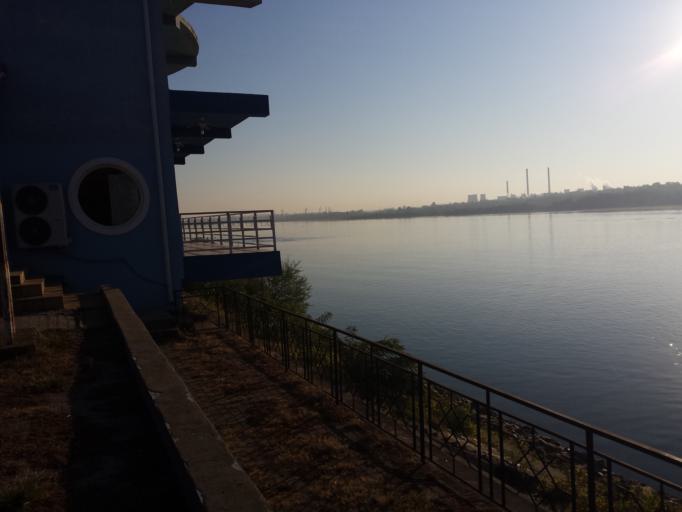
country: RO
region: Giurgiu
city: Giurgiu
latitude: 43.8702
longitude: 25.9663
